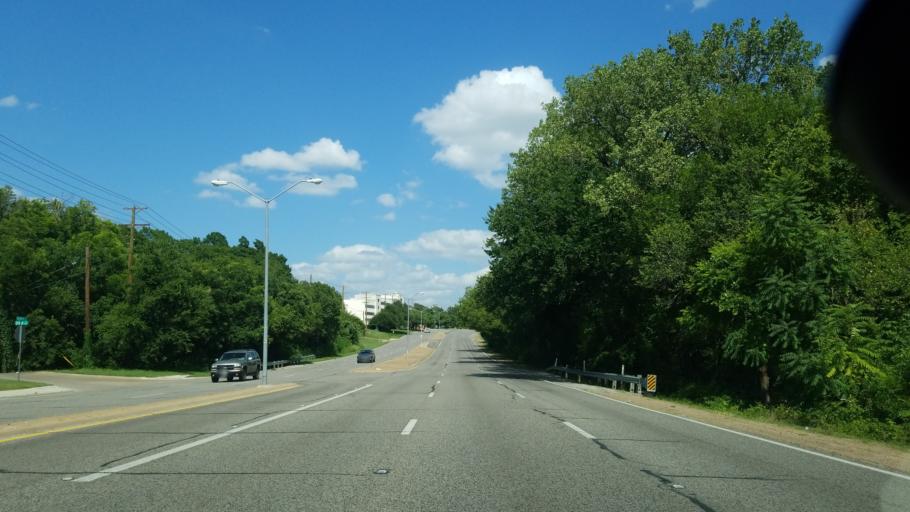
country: US
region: Texas
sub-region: Dallas County
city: Balch Springs
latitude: 32.7633
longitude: -96.6963
